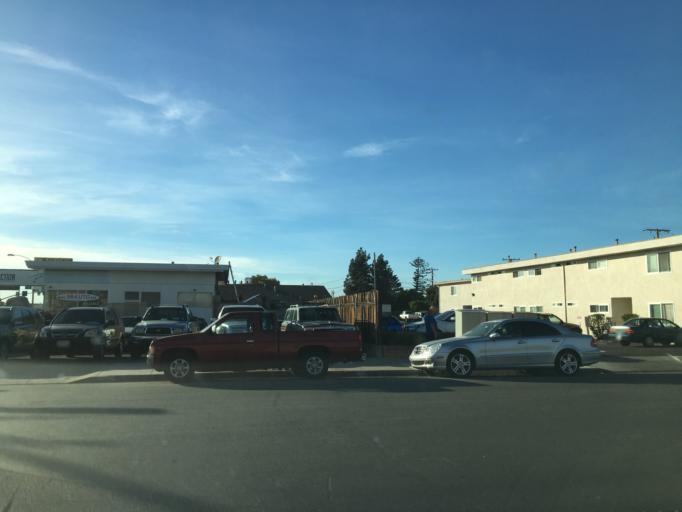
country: US
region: California
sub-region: Santa Barbara County
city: Goleta
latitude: 34.4360
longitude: -119.8222
